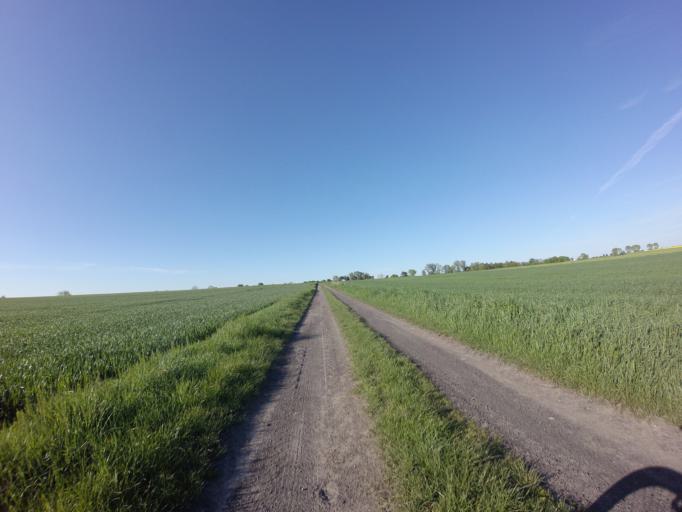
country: PL
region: West Pomeranian Voivodeship
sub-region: Powiat choszczenski
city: Choszczno
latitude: 53.1211
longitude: 15.3681
